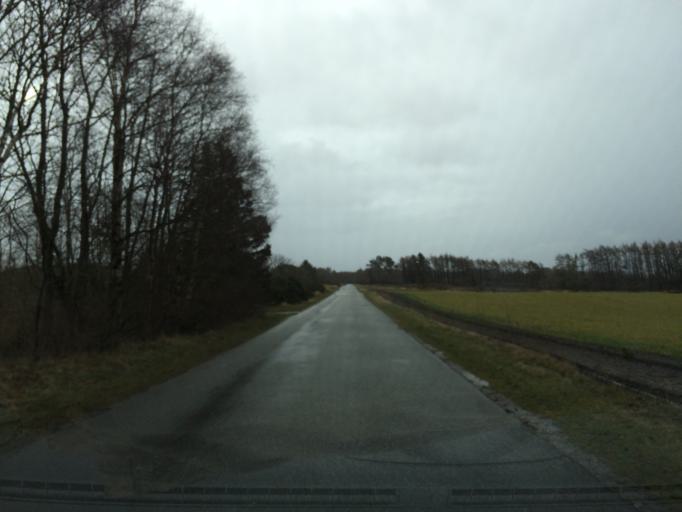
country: DK
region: Central Jutland
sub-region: Ringkobing-Skjern Kommune
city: Videbaek
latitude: 56.2124
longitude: 8.5369
